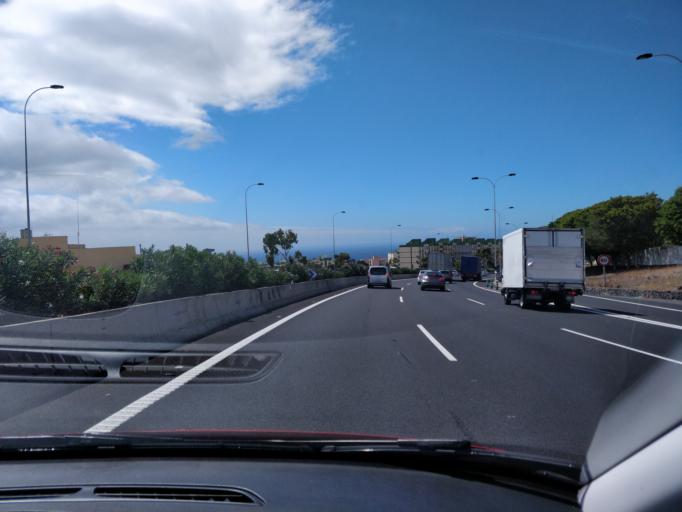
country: ES
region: Canary Islands
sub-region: Provincia de Santa Cruz de Tenerife
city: Santa Cruz de Tenerife
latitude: 28.4538
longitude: -16.2914
